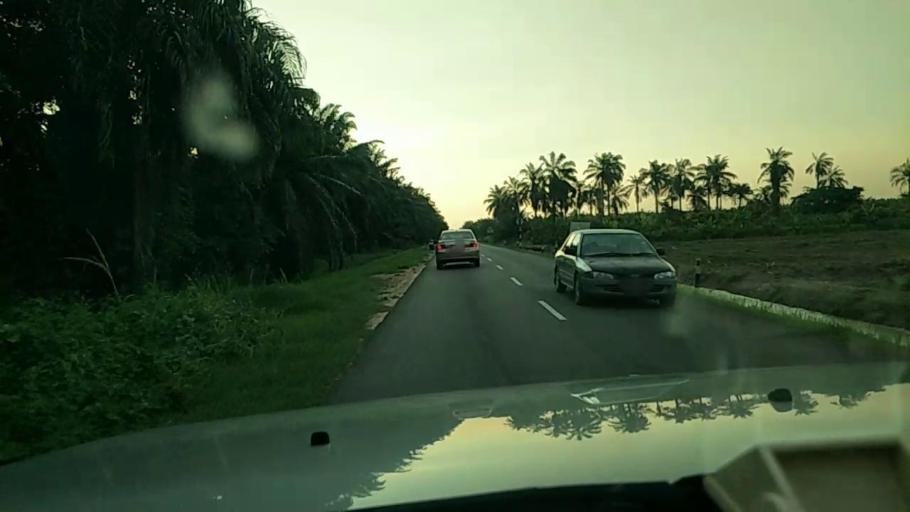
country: MY
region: Selangor
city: Kuala Selangor
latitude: 3.3167
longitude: 101.2809
